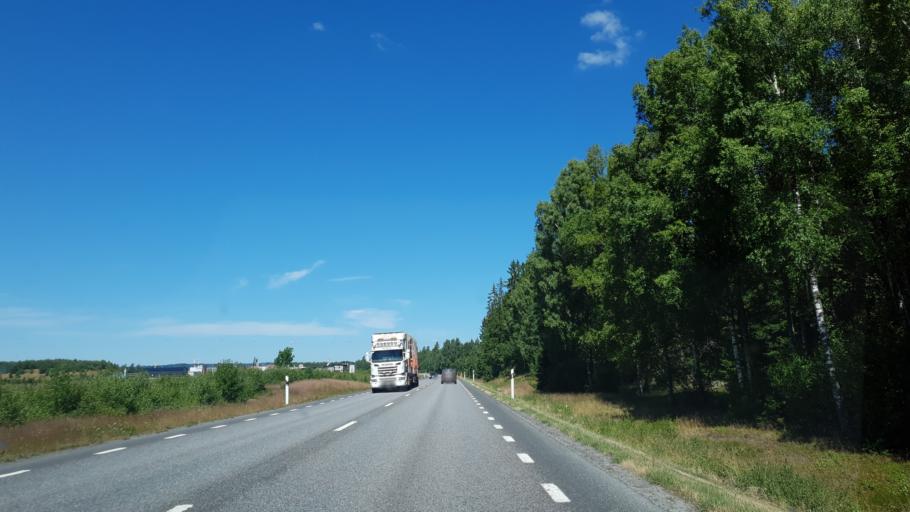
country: SE
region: Joenkoeping
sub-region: Varnamo Kommun
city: Varnamo
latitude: 57.1561
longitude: 14.0865
